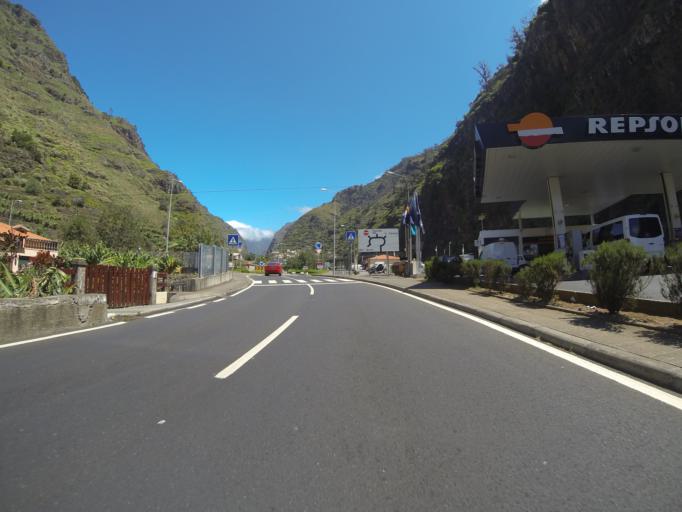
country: PT
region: Madeira
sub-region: Ribeira Brava
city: Campanario
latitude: 32.6819
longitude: -17.0521
